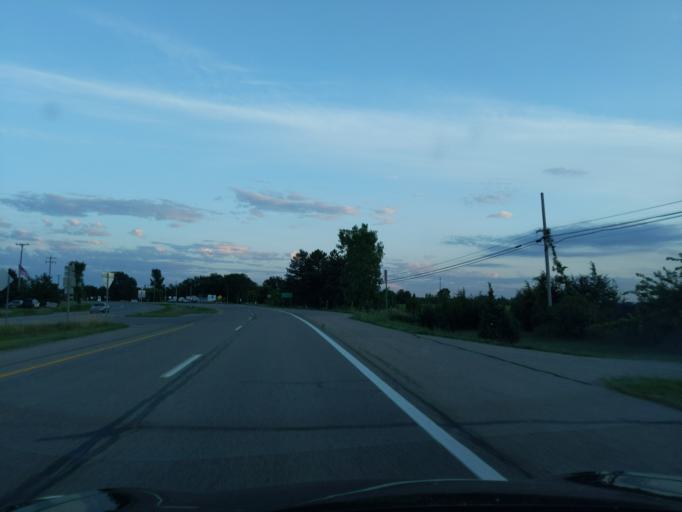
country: US
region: Michigan
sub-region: Clinton County
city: Saint Johns
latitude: 43.0202
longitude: -84.5632
